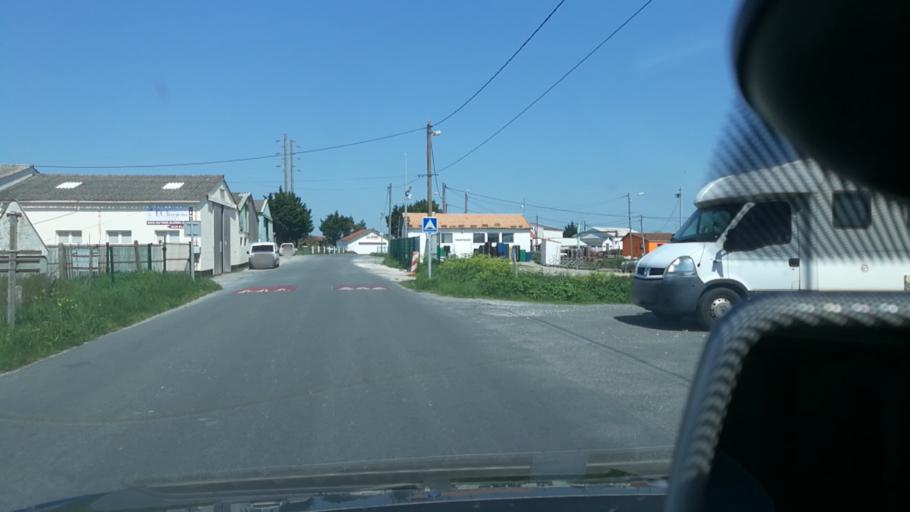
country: FR
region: Poitou-Charentes
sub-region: Departement de la Charente-Maritime
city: Saint-Trojan-les-Bains
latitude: 45.8697
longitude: -1.2193
